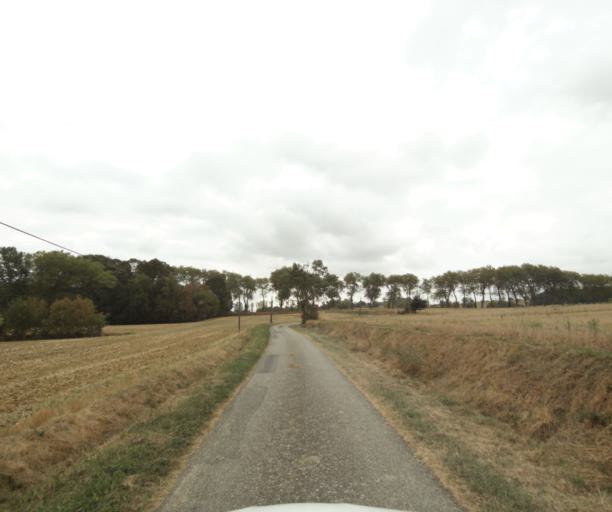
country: FR
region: Midi-Pyrenees
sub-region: Departement de la Haute-Garonne
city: Villefranche-de-Lauragais
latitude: 43.4156
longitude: 1.7379
